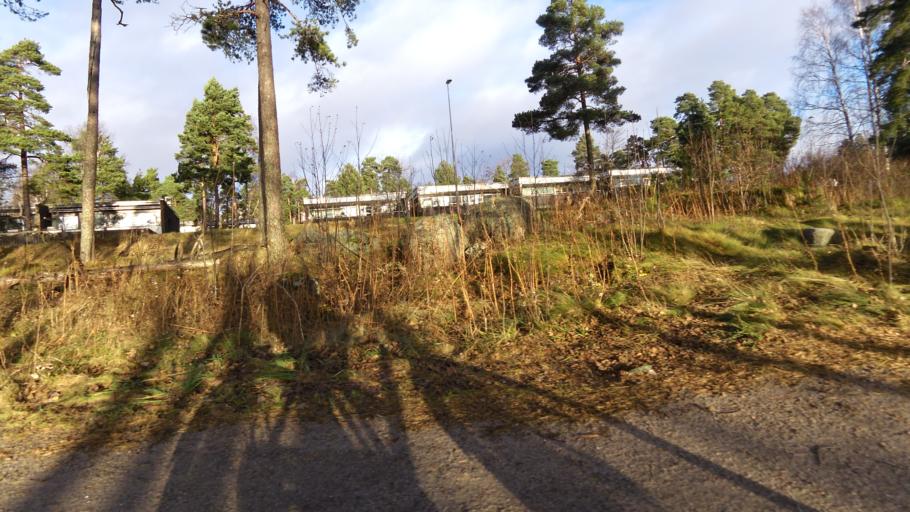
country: FI
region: Uusimaa
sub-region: Helsinki
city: Koukkuniemi
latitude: 60.1554
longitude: 24.7796
